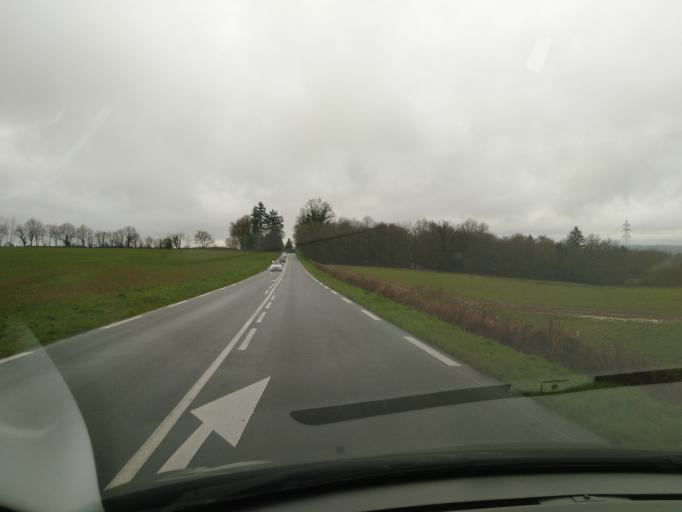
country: FR
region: Limousin
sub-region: Departement de la Haute-Vienne
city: Condat-sur-Vienne
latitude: 45.7756
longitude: 1.2891
